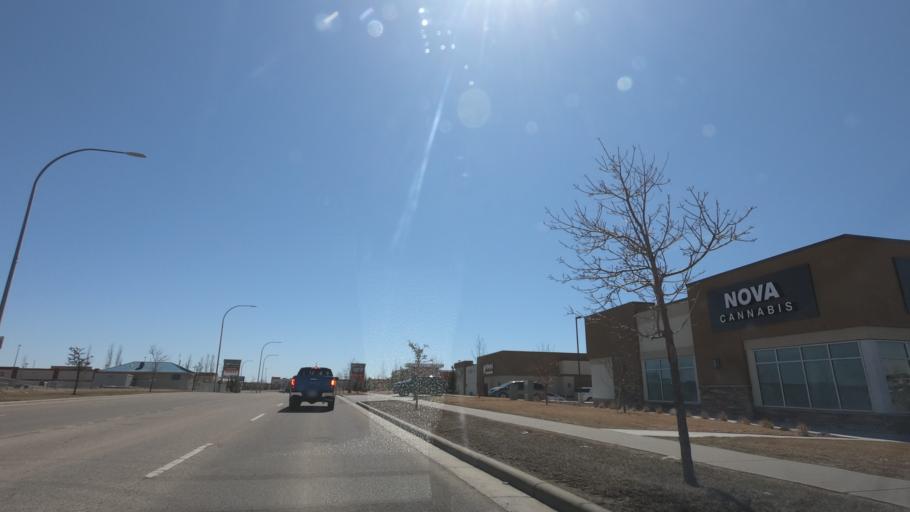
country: CA
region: Alberta
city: Airdrie
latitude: 51.2664
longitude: -114.0071
